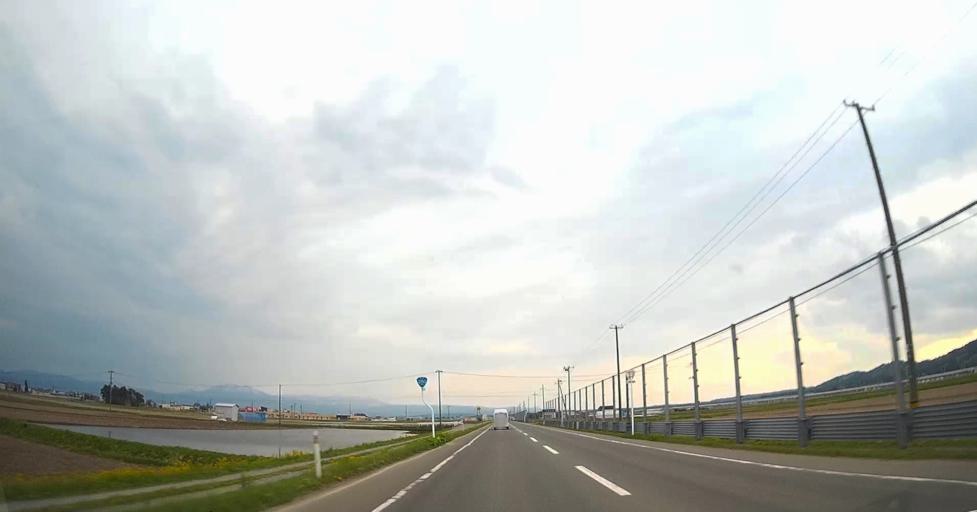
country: JP
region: Aomori
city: Aomori Shi
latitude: 40.8917
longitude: 140.6687
